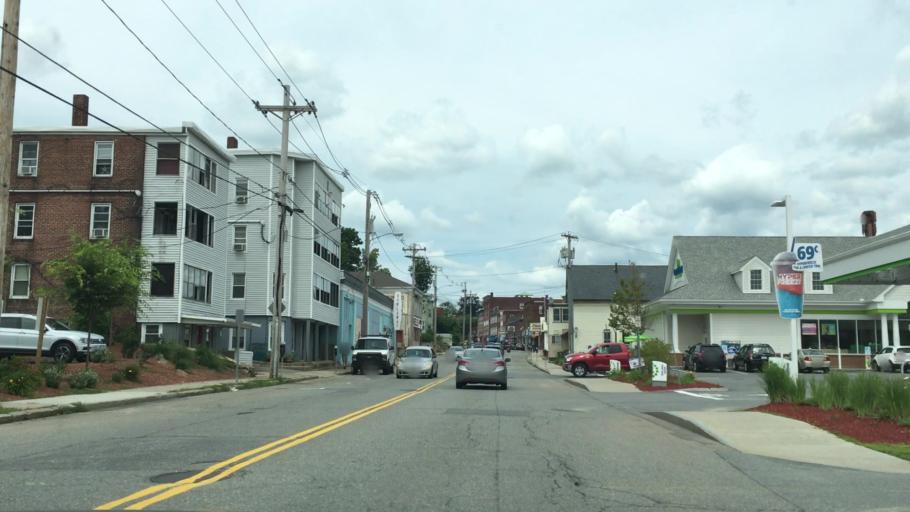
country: US
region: Massachusetts
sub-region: Worcester County
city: Gardner
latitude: 42.5728
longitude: -71.9944
